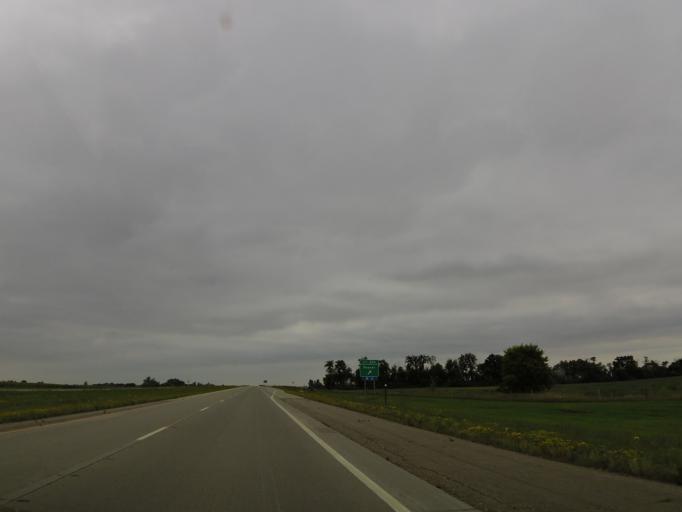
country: US
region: South Dakota
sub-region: Roberts County
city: Sisseton
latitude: 45.5379
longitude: -96.9892
